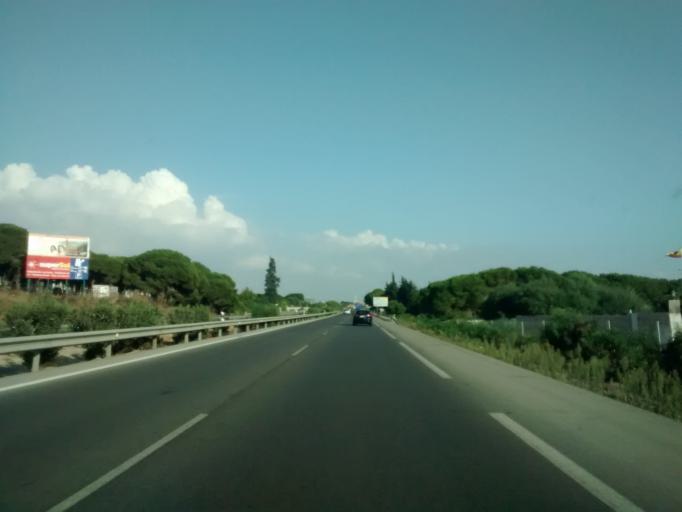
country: ES
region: Andalusia
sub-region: Provincia de Cadiz
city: Chiclana de la Frontera
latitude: 36.4432
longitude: -6.1351
